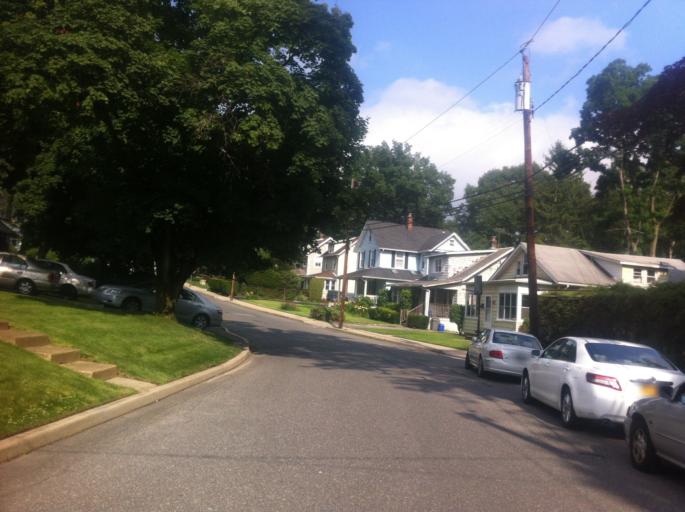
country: US
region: New York
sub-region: Nassau County
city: Glen Head
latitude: 40.8485
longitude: -73.6294
